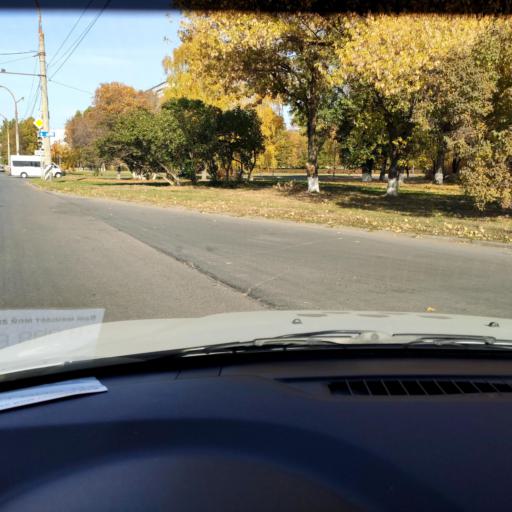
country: RU
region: Samara
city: Tol'yatti
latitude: 53.5159
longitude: 49.2582
